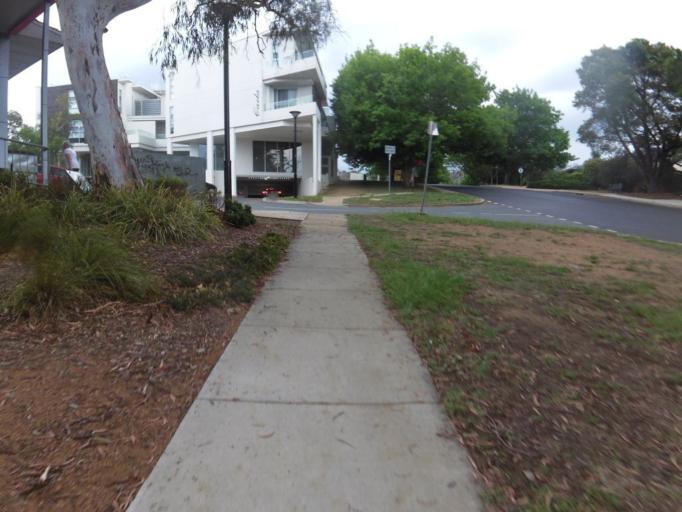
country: AU
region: Australian Capital Territory
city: Forrest
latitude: -35.3408
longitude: 149.1314
